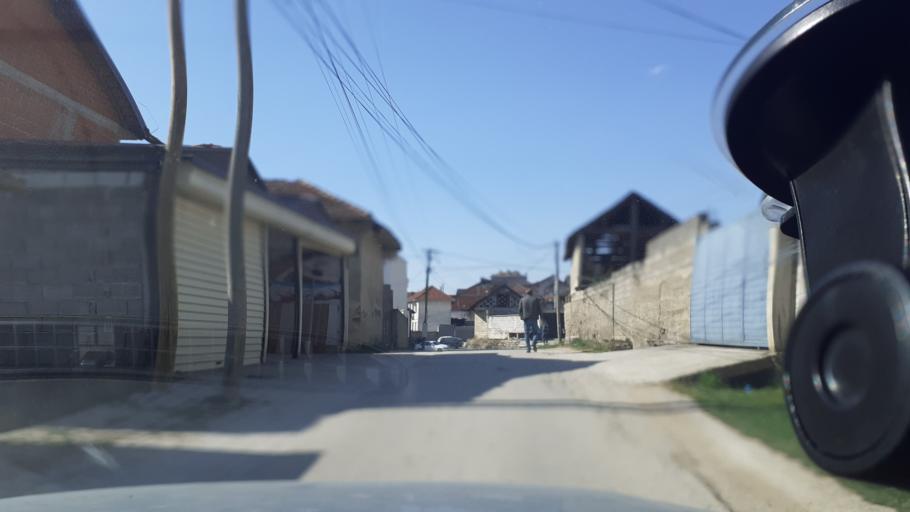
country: MK
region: Tearce
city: Slatino
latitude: 42.0685
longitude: 21.0391
